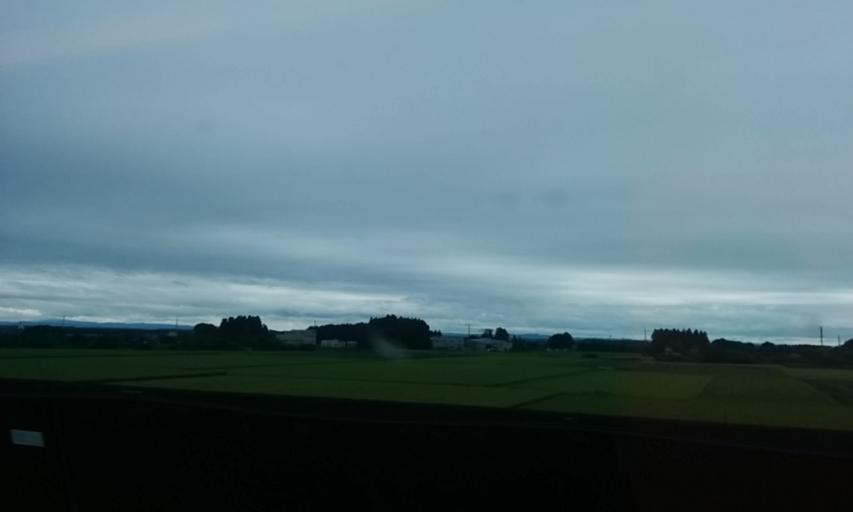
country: JP
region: Tochigi
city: Ujiie
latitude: 36.6666
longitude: 139.9146
